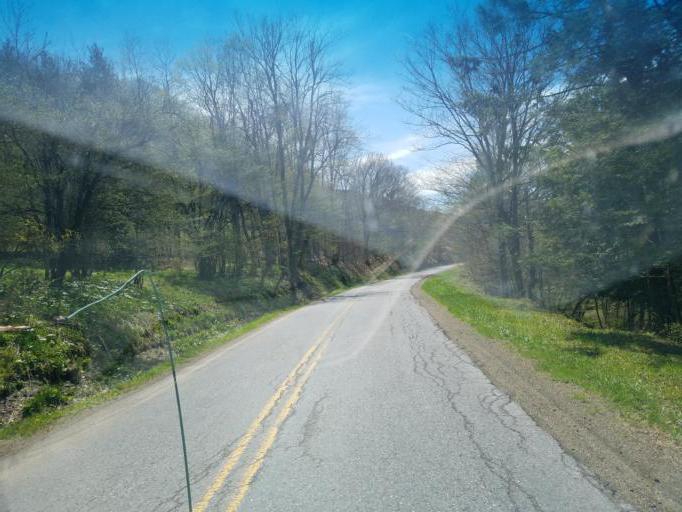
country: US
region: Pennsylvania
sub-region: Potter County
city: Galeton
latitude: 41.8650
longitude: -77.7180
